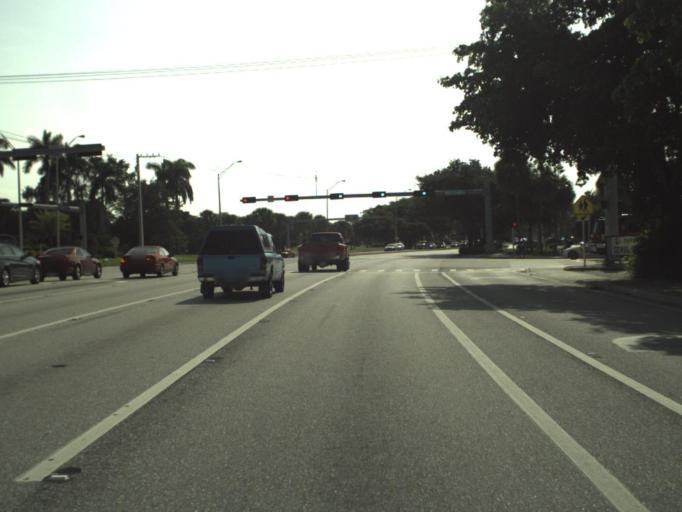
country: US
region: Florida
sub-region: Broward County
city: Margate
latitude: 26.2724
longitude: -80.2223
